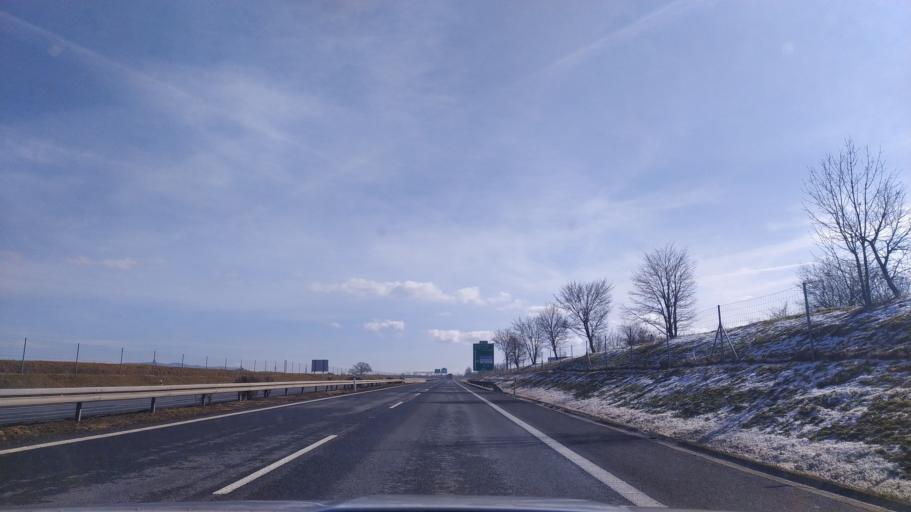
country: CZ
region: Karlovarsky
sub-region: Okres Cheb
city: Cheb
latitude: 50.0938
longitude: 12.4116
